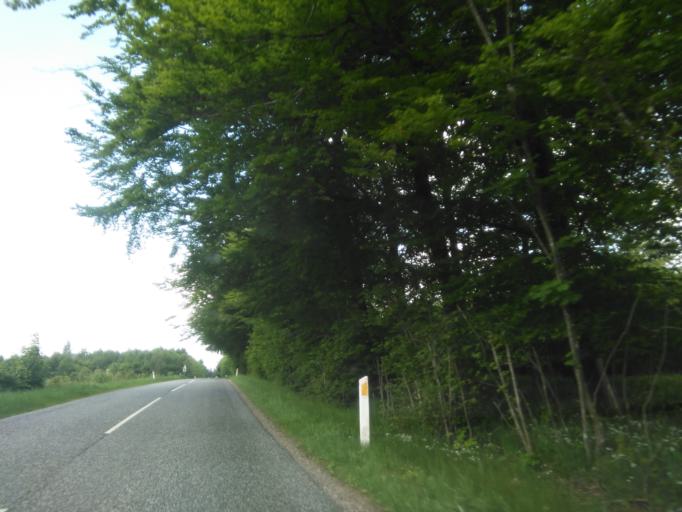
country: DK
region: Central Jutland
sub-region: Favrskov Kommune
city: Hammel
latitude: 56.2518
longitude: 9.9140
